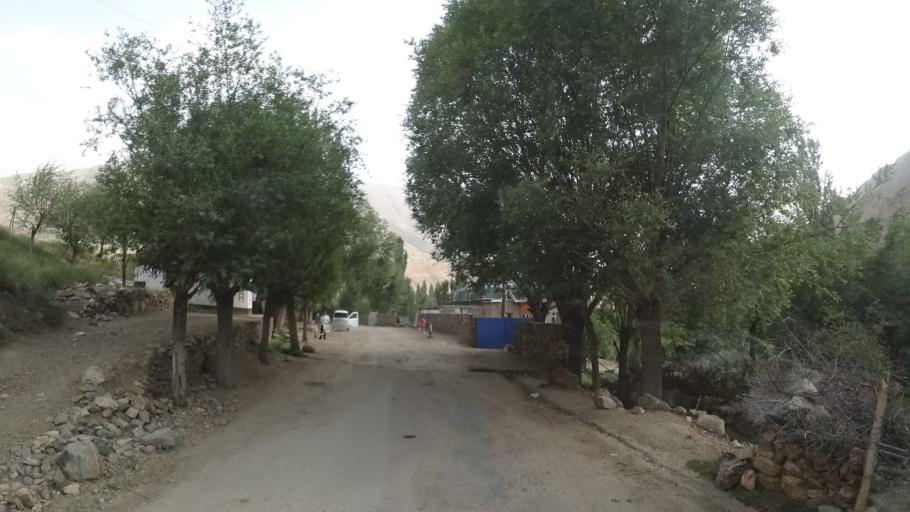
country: TJ
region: Gorno-Badakhshan
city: Khorugh
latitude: 37.2377
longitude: 71.4843
